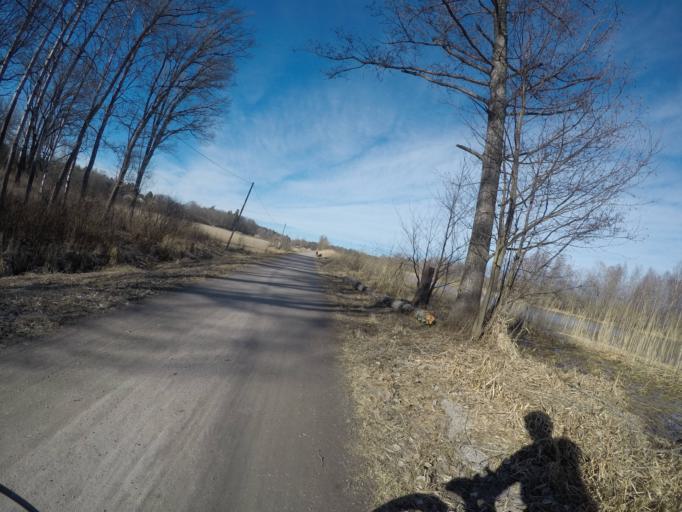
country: SE
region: Soedermanland
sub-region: Eskilstuna Kommun
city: Torshalla
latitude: 59.4107
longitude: 16.4642
